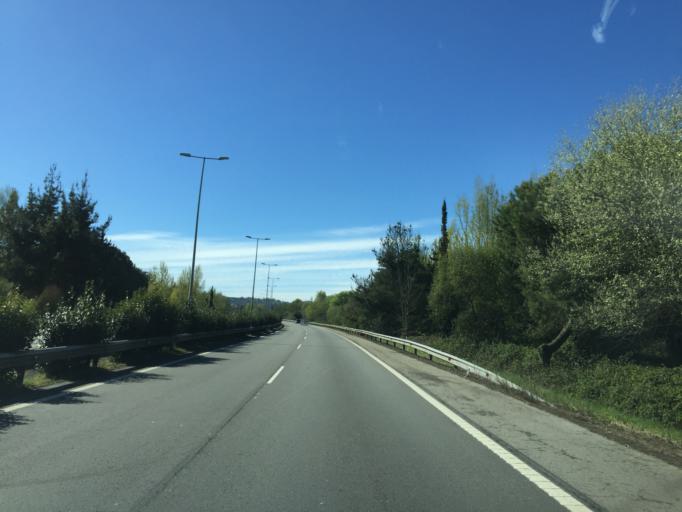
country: ES
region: Asturias
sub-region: Province of Asturias
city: Lugones
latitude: 43.3827
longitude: -5.8124
